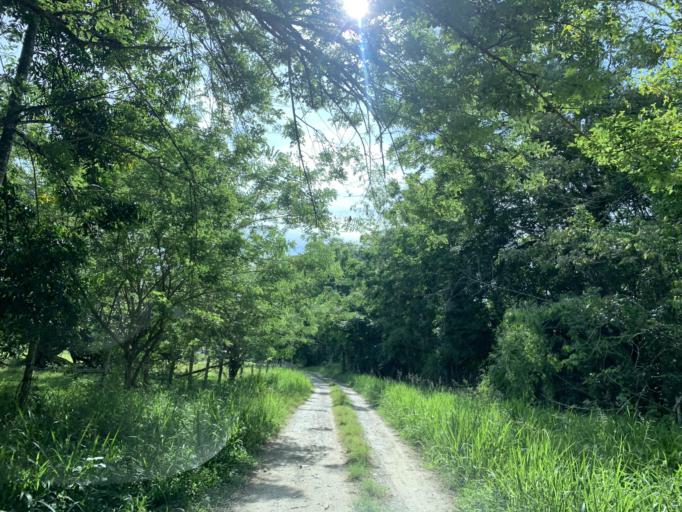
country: CO
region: Boyaca
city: Puerto Boyaca
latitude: 6.0112
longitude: -74.3920
